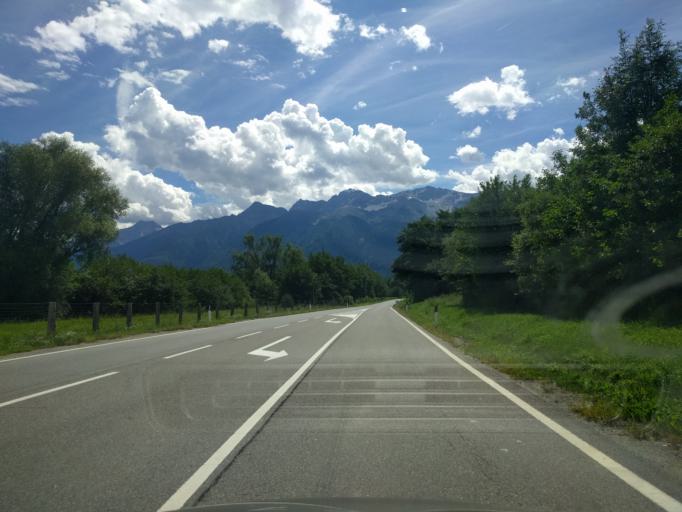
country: IT
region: Trentino-Alto Adige
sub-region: Bolzano
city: Glorenza
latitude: 46.6580
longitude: 10.5642
